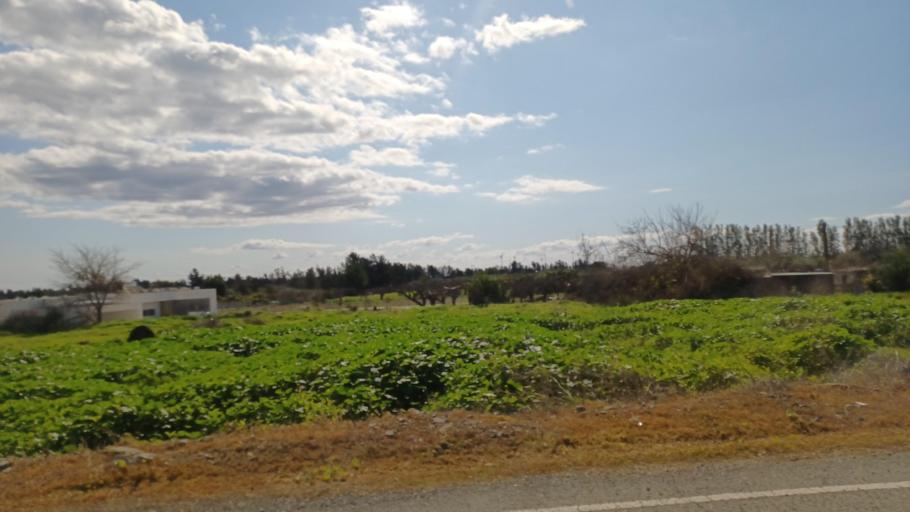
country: CY
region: Pafos
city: Paphos
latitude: 34.7530
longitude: 32.4418
